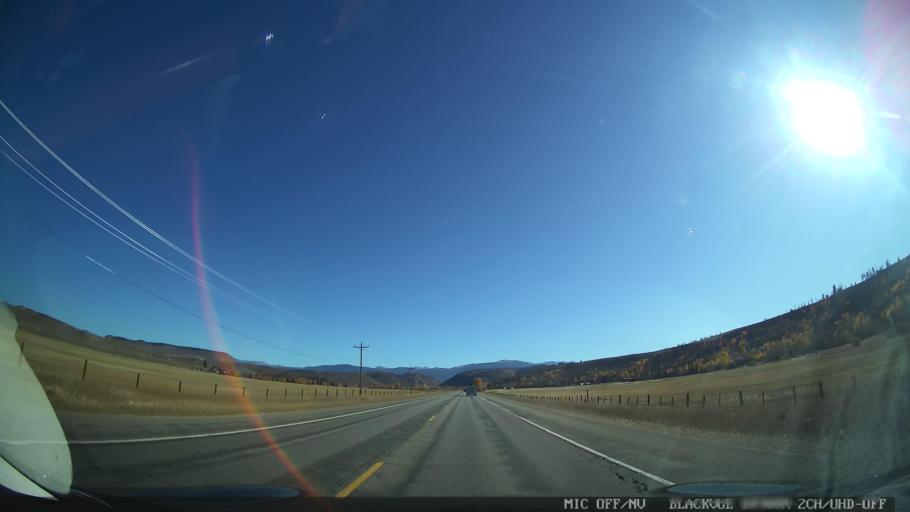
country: US
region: Colorado
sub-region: Grand County
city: Granby
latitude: 40.1121
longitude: -105.9221
